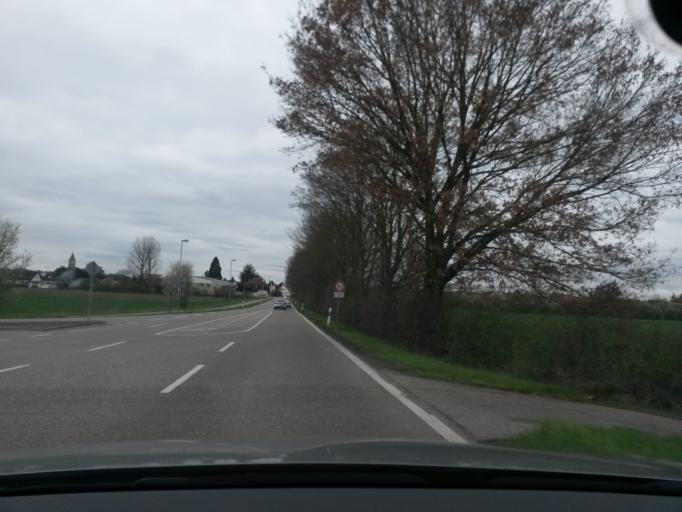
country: DE
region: Baden-Wuerttemberg
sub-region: Karlsruhe Region
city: Kronau
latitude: 49.2213
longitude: 8.6435
